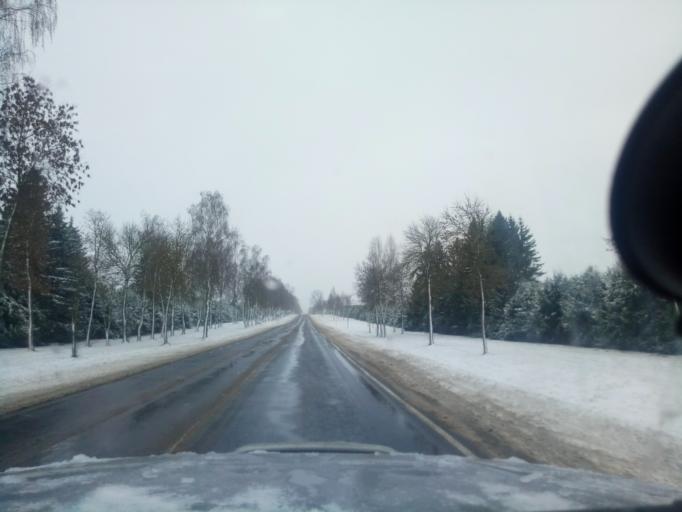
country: BY
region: Minsk
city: Haradzyeya
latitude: 53.3589
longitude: 26.5146
